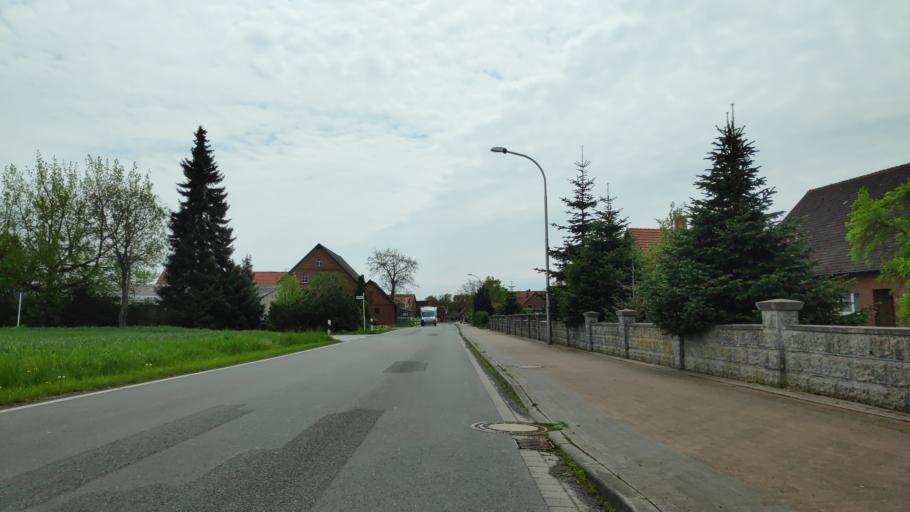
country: DE
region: North Rhine-Westphalia
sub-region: Regierungsbezirk Detmold
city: Petershagen
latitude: 52.3201
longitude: 8.9950
